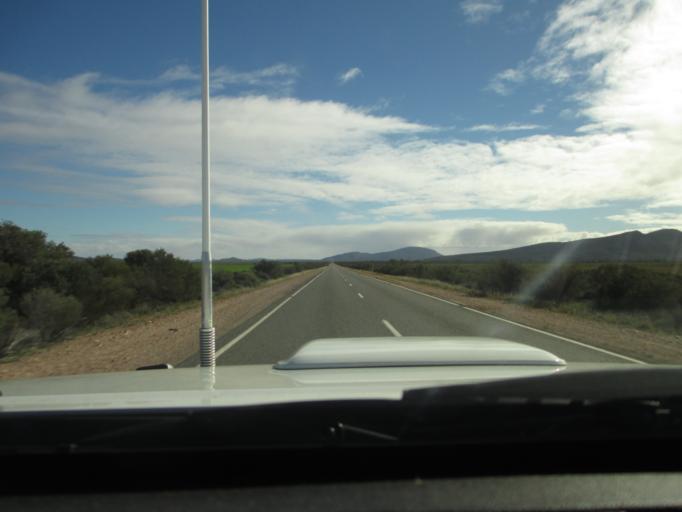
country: AU
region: South Australia
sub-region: Flinders Ranges
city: Quorn
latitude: -31.8690
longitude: 138.4075
